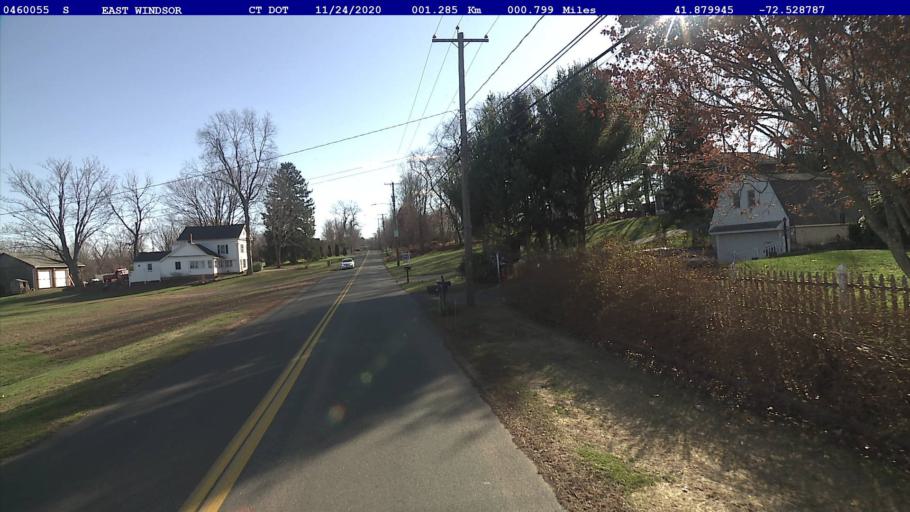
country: US
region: Connecticut
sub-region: Hartford County
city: Broad Brook
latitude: 41.8800
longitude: -72.5288
